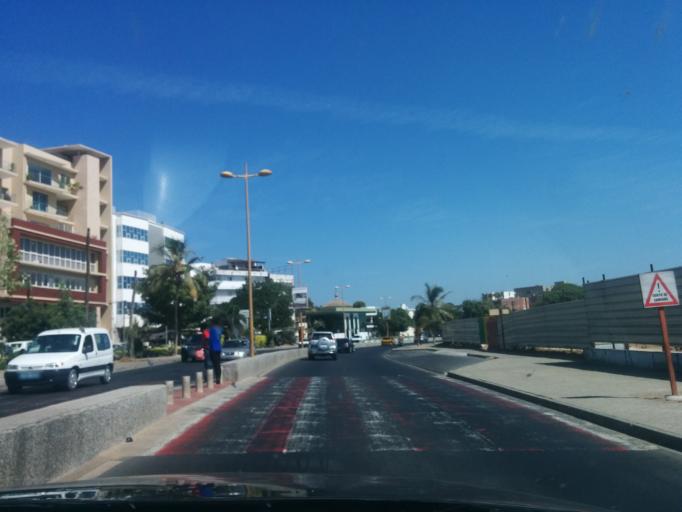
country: SN
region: Dakar
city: Dakar
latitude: 14.6787
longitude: -17.4625
